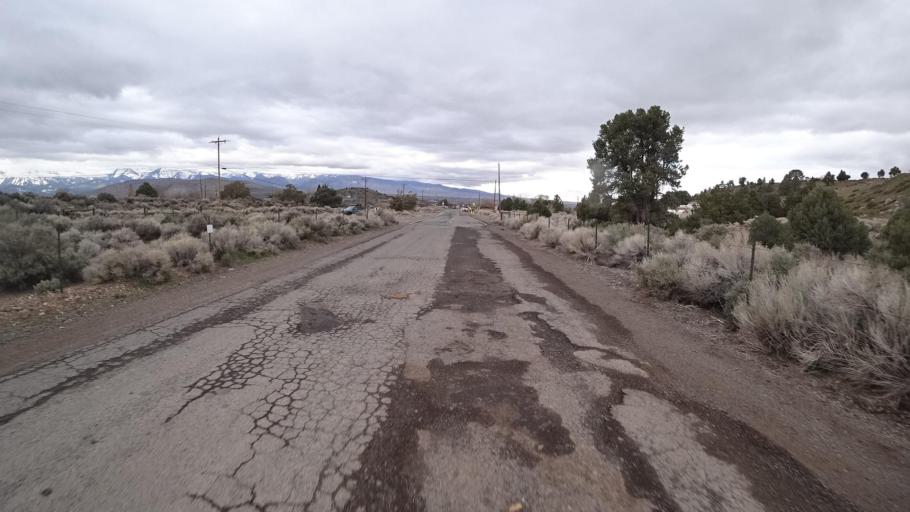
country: US
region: Nevada
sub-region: Storey County
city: Virginia City
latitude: 39.3750
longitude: -119.7147
